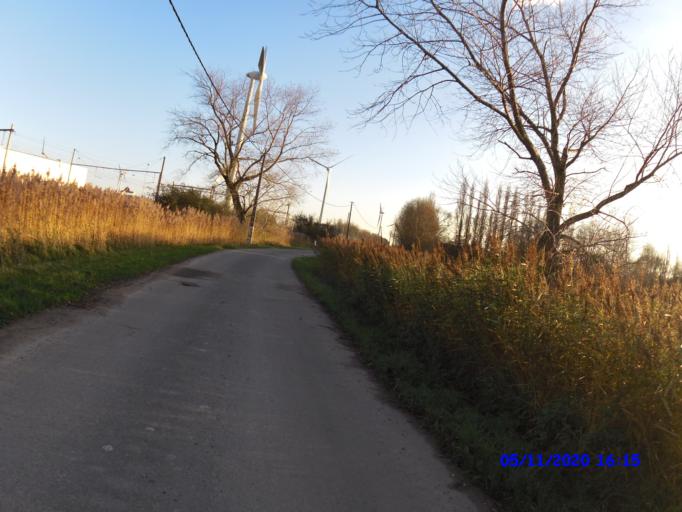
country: BE
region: Flanders
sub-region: Provincie West-Vlaanderen
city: Zuienkerke
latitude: 51.2599
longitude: 3.2026
